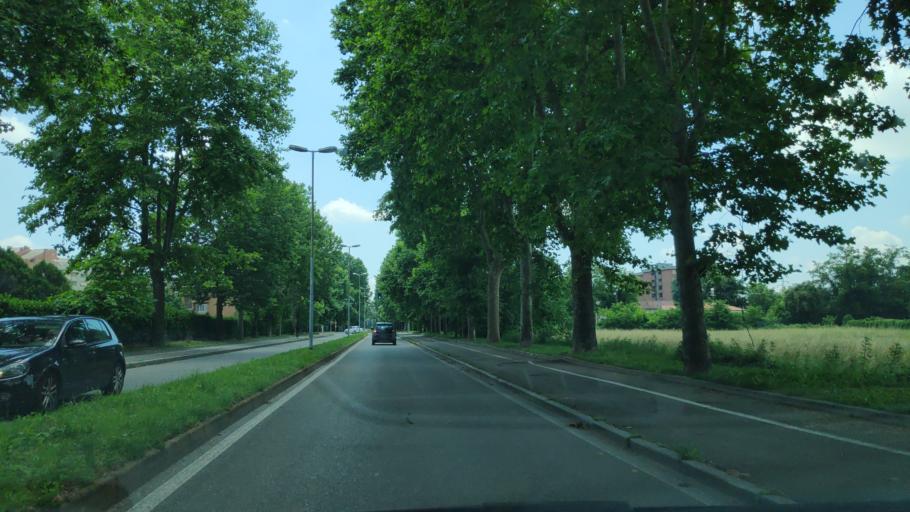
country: IT
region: Lombardy
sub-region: Provincia di Monza e Brianza
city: Villasanta
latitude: 45.5885
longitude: 9.2986
